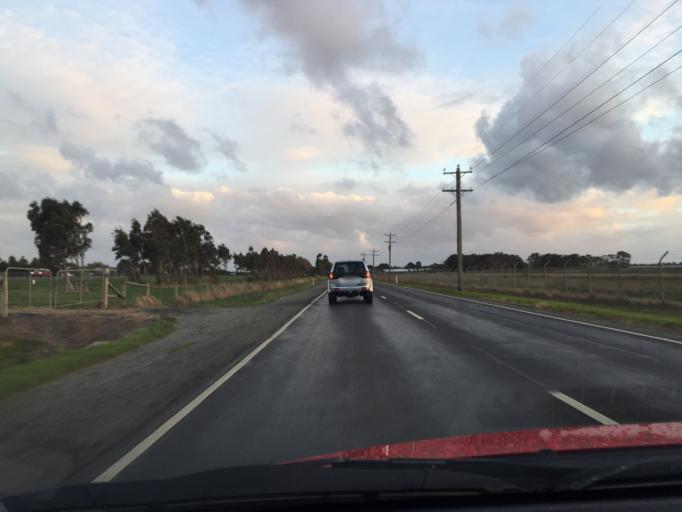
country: AU
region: Victoria
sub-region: Frankston
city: Sandhurst
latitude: -38.0565
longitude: 145.1837
